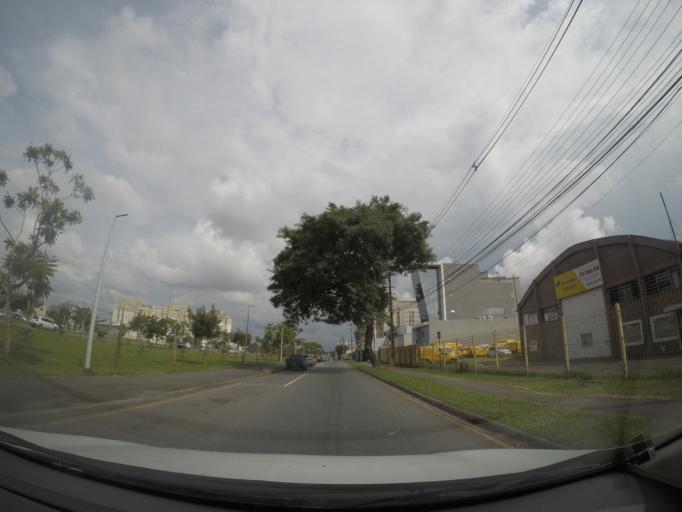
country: BR
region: Parana
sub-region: Curitiba
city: Curitiba
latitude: -25.4907
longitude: -49.2718
